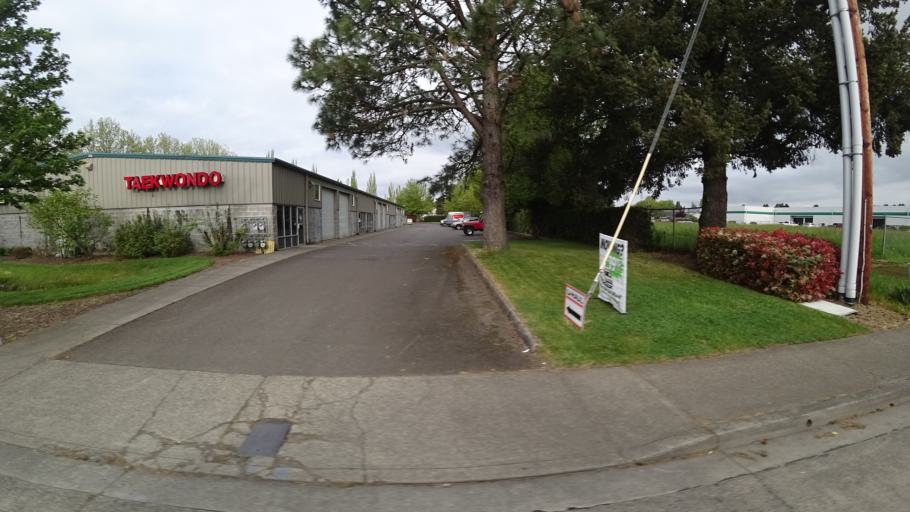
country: US
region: Oregon
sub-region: Washington County
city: Hillsboro
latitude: 45.5331
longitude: -122.9570
